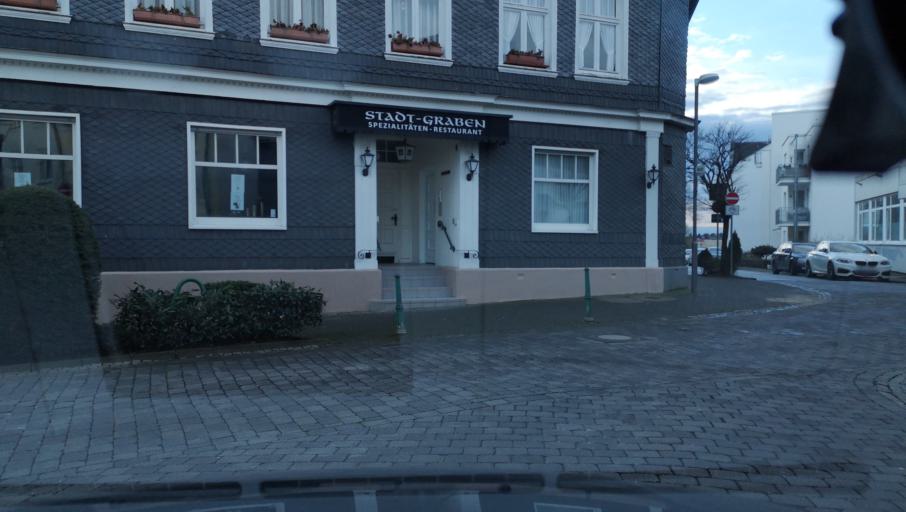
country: DE
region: North Rhine-Westphalia
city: Radevormwald
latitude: 51.2025
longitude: 7.3555
